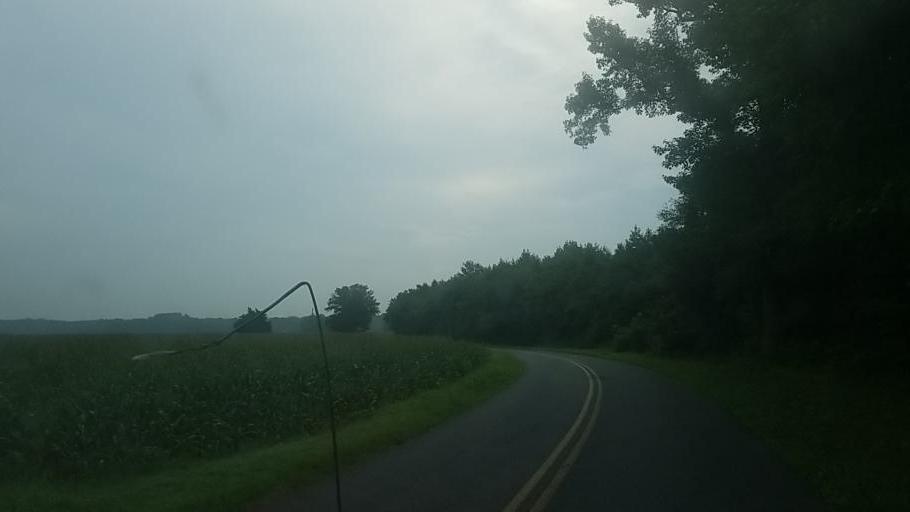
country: US
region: Delaware
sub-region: Sussex County
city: Selbyville
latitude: 38.4255
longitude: -75.2980
